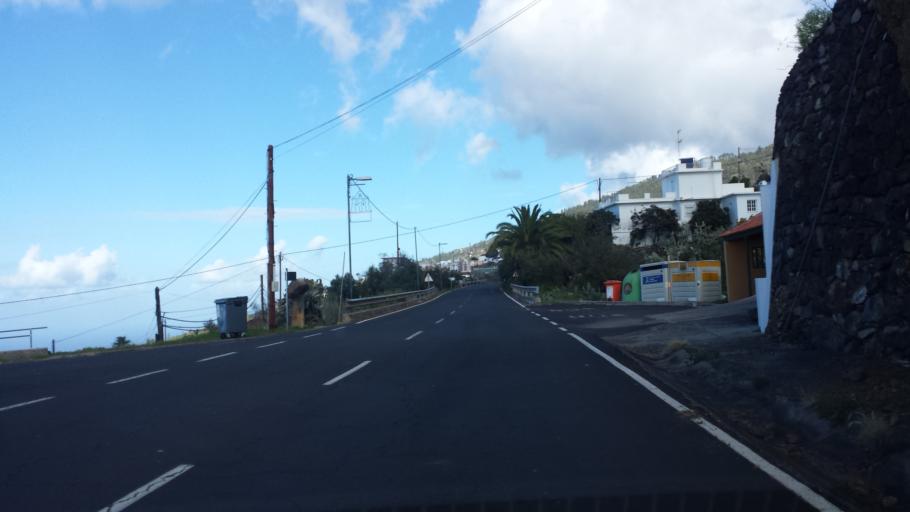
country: ES
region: Canary Islands
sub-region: Provincia de Santa Cruz de Tenerife
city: Tijarafe
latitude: 28.7009
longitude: -17.9510
